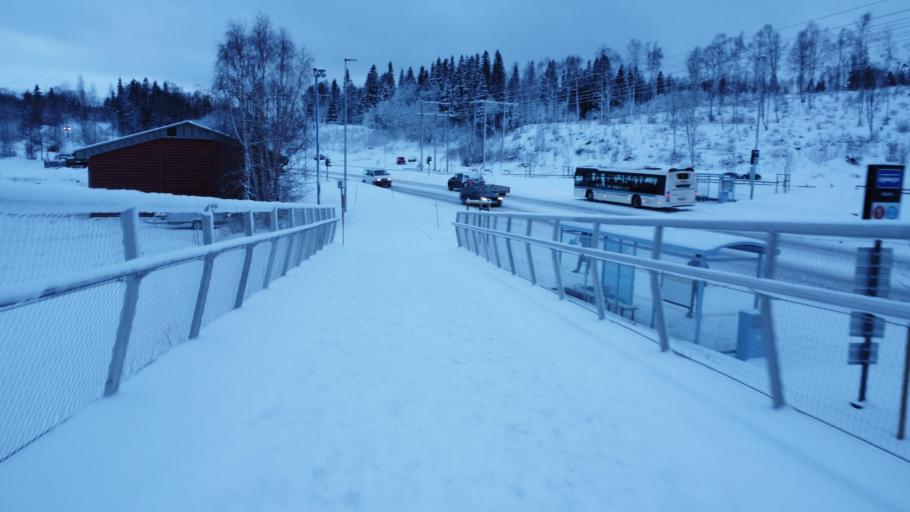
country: NO
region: Nordland
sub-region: Rana
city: Mo i Rana
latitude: 66.3293
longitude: 14.1612
